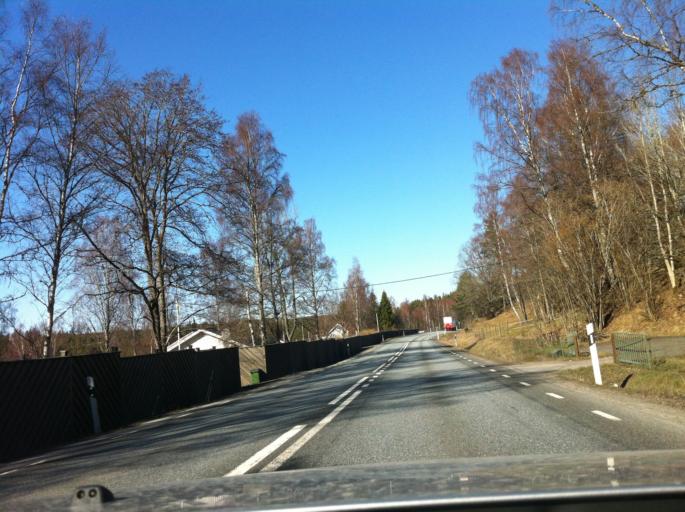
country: SE
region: Joenkoeping
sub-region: Mullsjo Kommun
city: Mullsjoe
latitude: 57.9673
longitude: 13.8314
